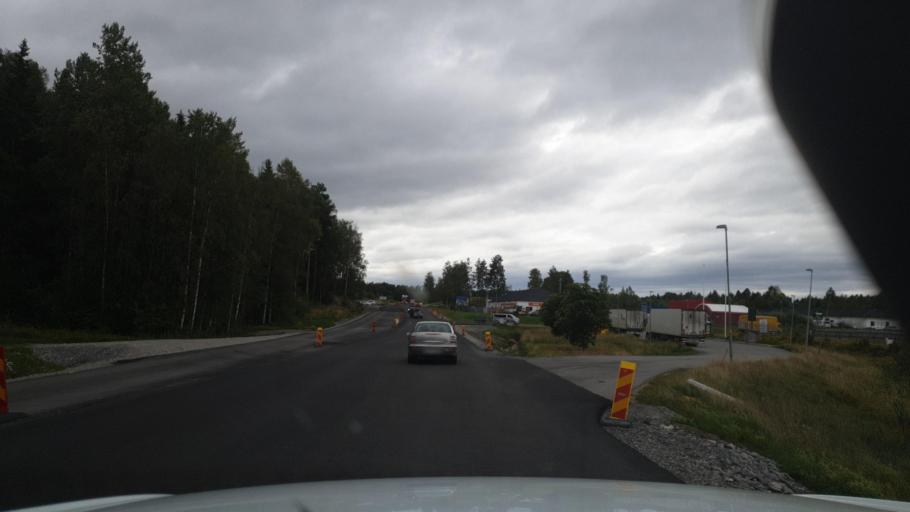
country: SE
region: Vaermland
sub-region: Arvika Kommun
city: Arvika
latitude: 59.6791
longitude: 12.5942
